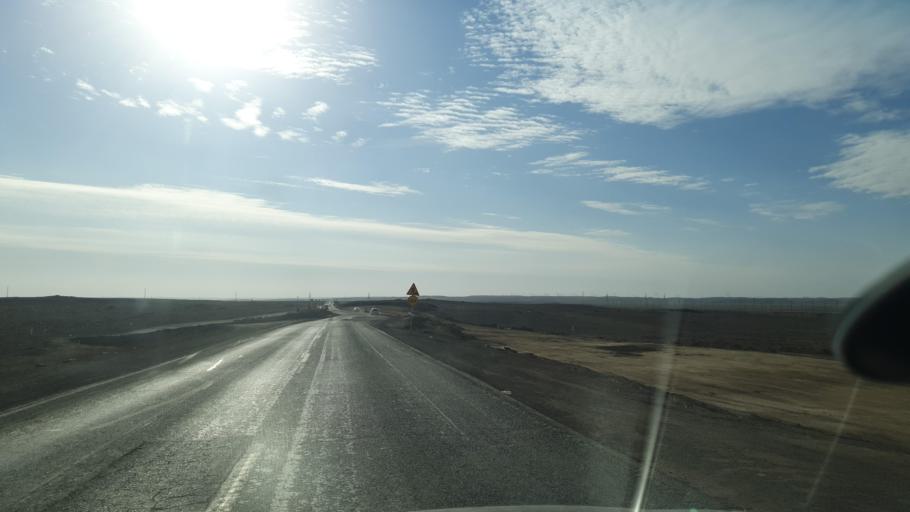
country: KZ
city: Priozersk
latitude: 45.8641
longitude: 73.4703
